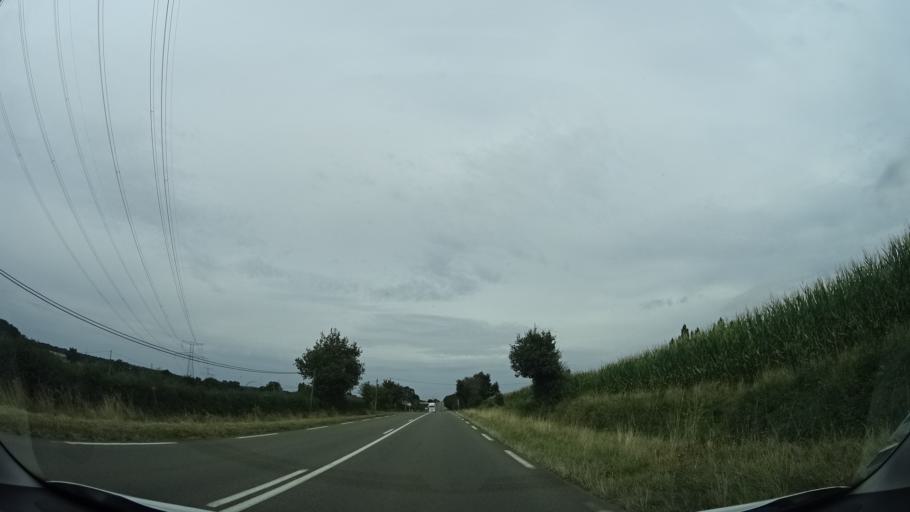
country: FR
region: Pays de la Loire
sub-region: Departement de la Sarthe
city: Auvers-le-Hamon
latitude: 47.9012
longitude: -0.4395
